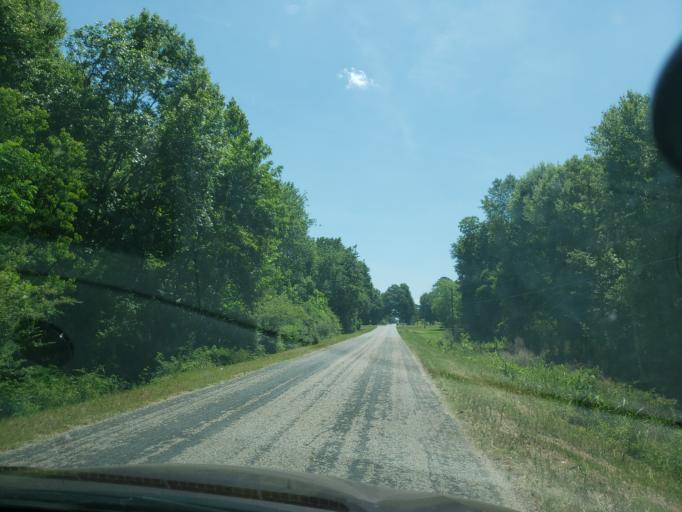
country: US
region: Alabama
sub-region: Elmore County
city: Tallassee
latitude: 32.5810
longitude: -85.8007
